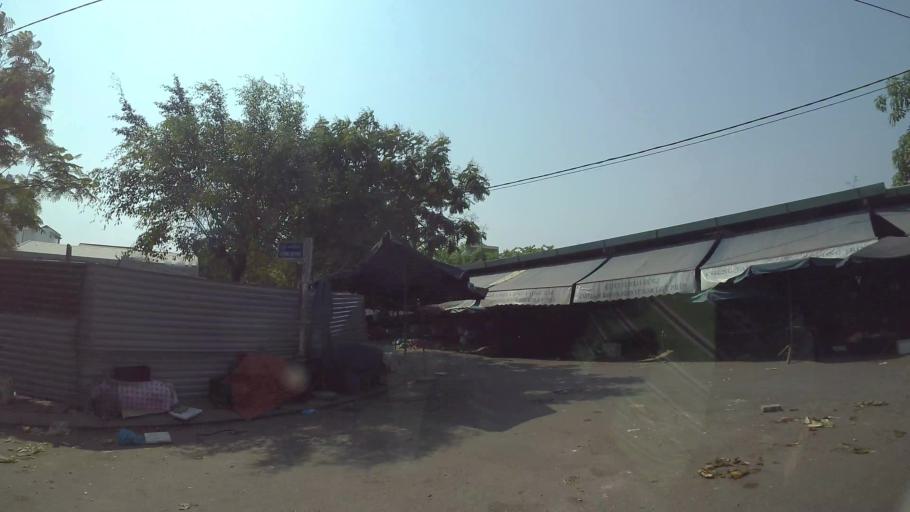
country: VN
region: Da Nang
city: Cam Le
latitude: 16.0108
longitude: 108.1978
